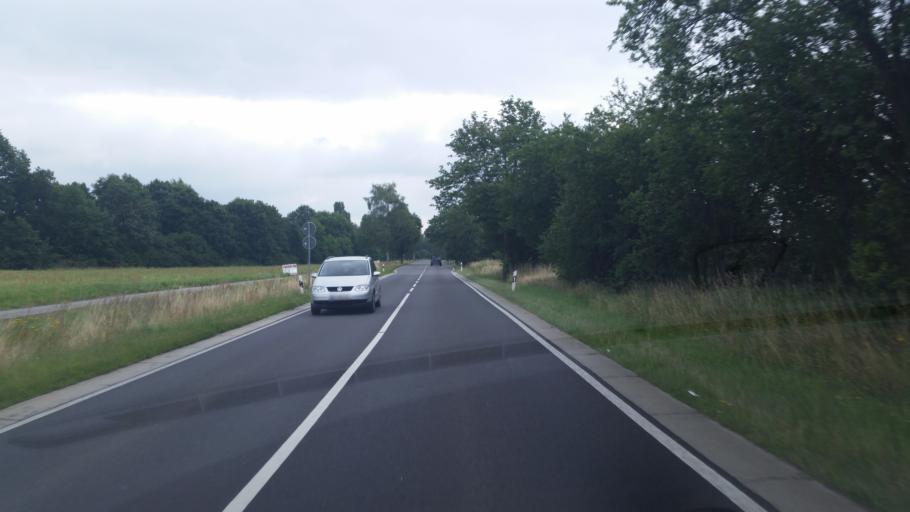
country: DE
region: Brandenburg
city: Senftenberg
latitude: 51.5133
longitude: 14.0326
